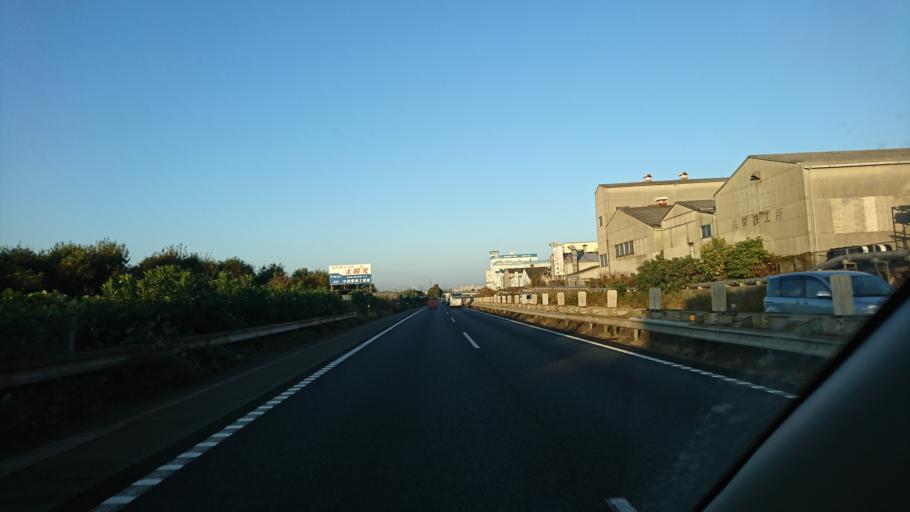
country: JP
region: Hyogo
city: Akashi
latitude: 34.7157
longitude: 134.9242
